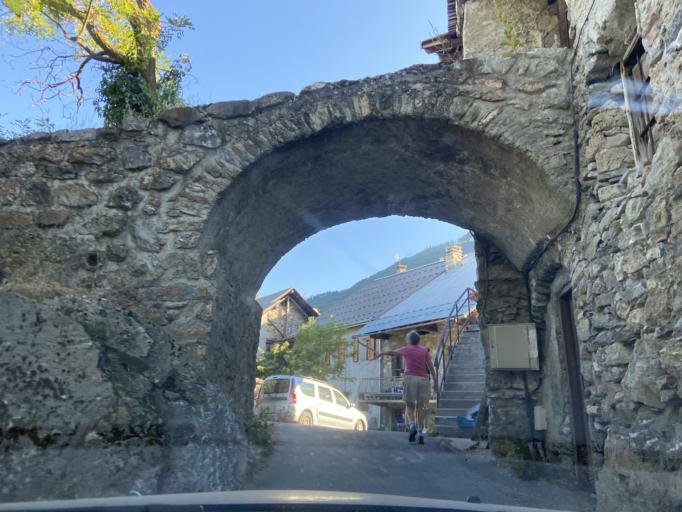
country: FR
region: Provence-Alpes-Cote d'Azur
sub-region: Departement des Hautes-Alpes
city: Guillestre
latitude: 44.7074
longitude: 6.5890
